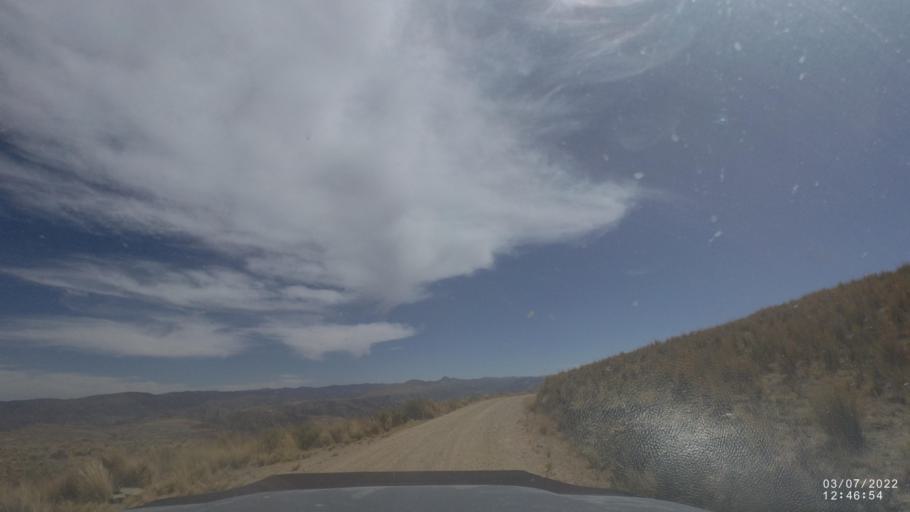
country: BO
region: Cochabamba
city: Irpa Irpa
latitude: -17.7714
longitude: -66.6399
